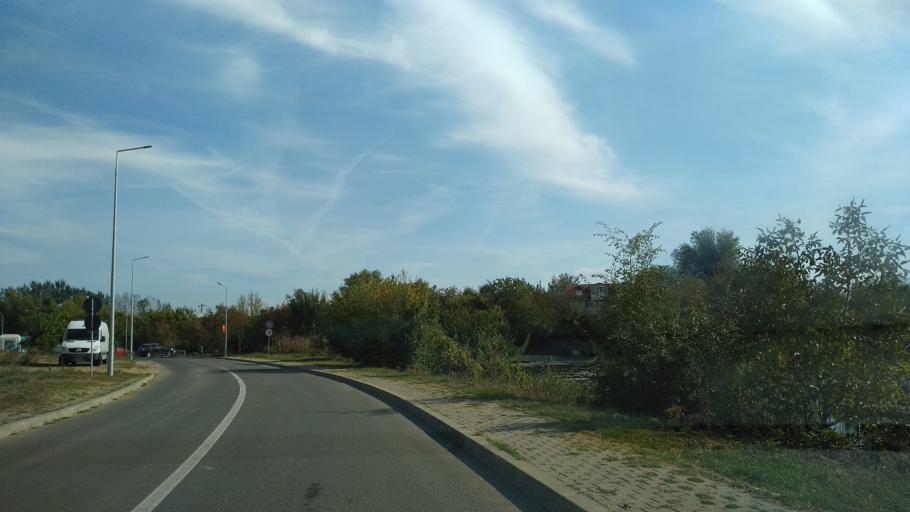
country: RO
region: Ilfov
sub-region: Comuna Chitila
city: Chitila
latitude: 44.5123
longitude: 25.9853
